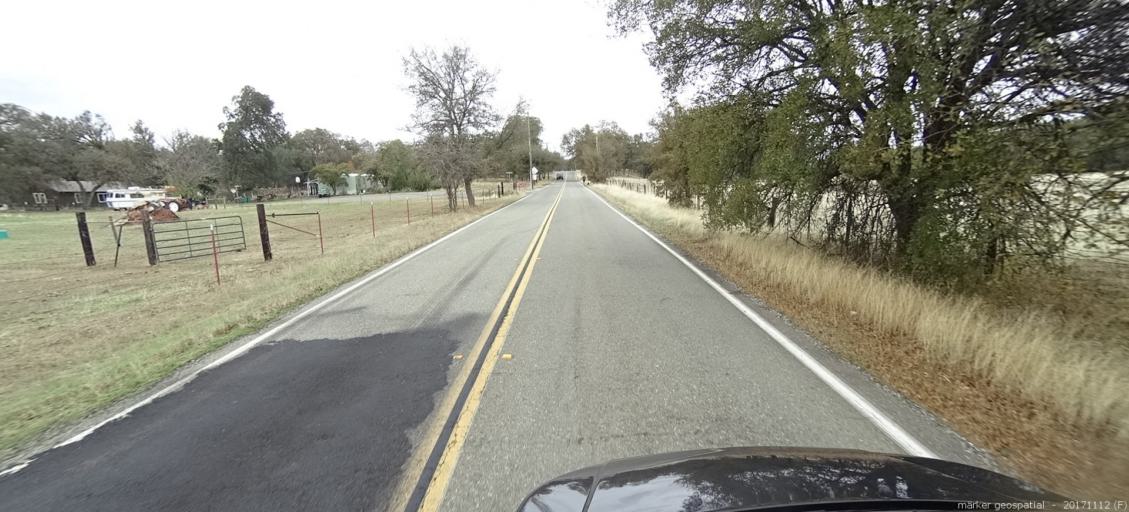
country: US
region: California
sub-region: Shasta County
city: Palo Cedro
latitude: 40.4820
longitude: -122.2056
